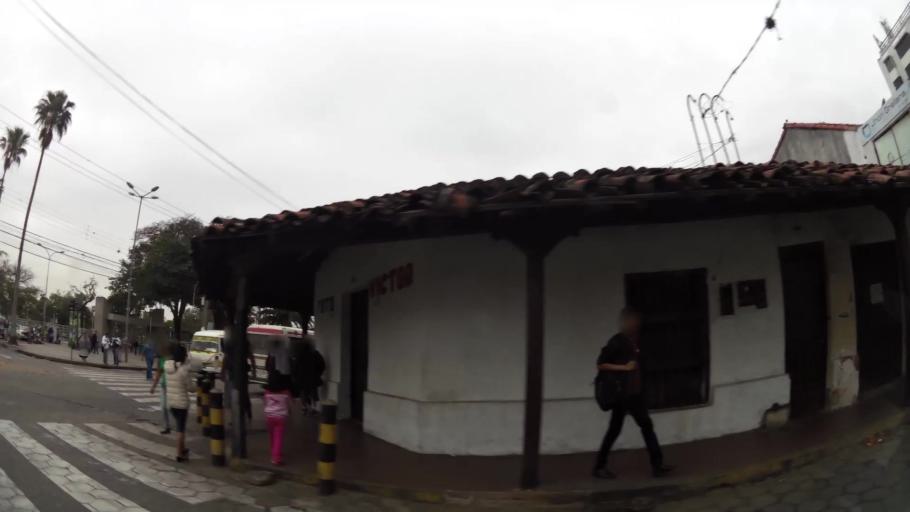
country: BO
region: Santa Cruz
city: Santa Cruz de la Sierra
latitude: -17.7795
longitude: -63.1809
